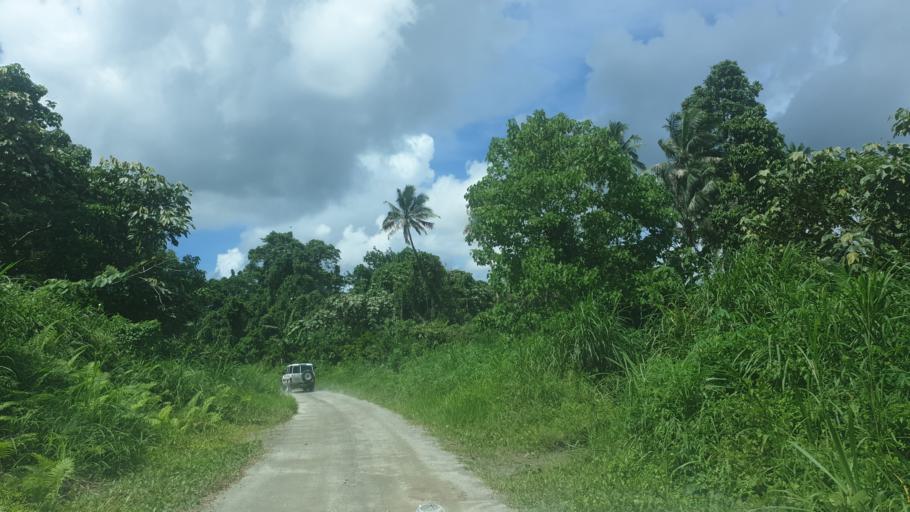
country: PG
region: Bougainville
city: Panguna
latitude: -6.7339
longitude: 155.4931
